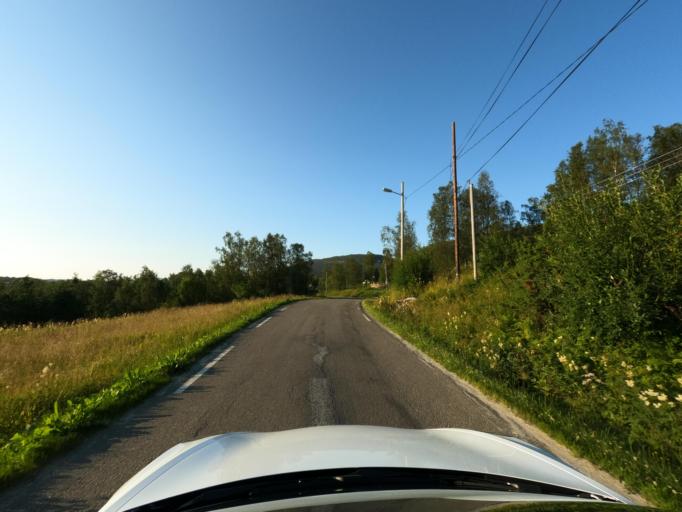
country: NO
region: Nordland
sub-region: Ballangen
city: Ballangen
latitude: 68.5252
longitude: 16.7660
